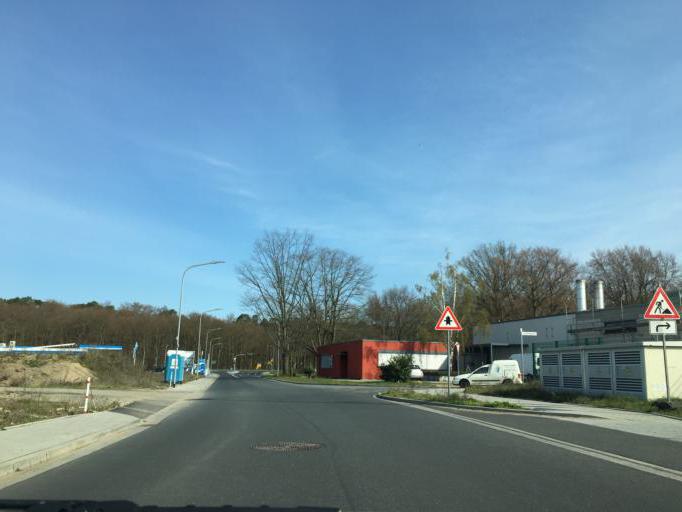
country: DE
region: Hesse
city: Obertshausen
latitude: 50.0613
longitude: 8.8307
